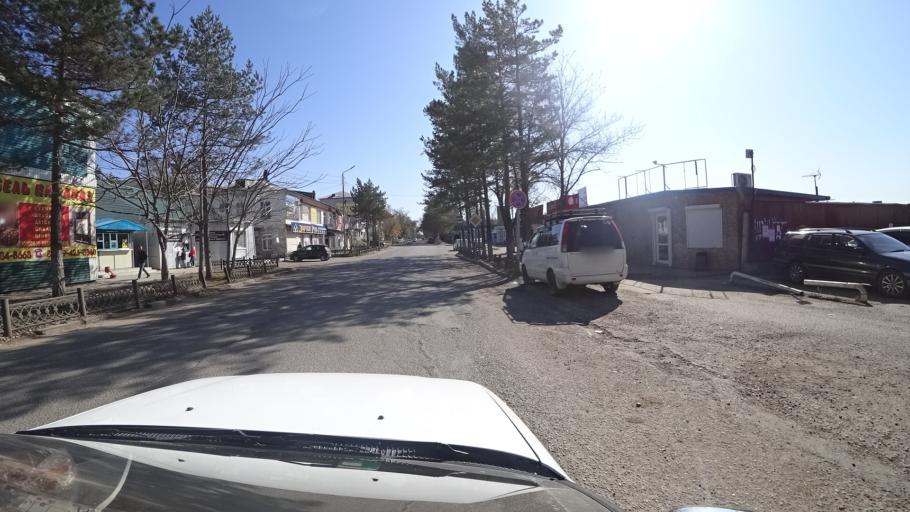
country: RU
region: Primorskiy
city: Dal'nerechensk
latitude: 45.9306
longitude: 133.7314
